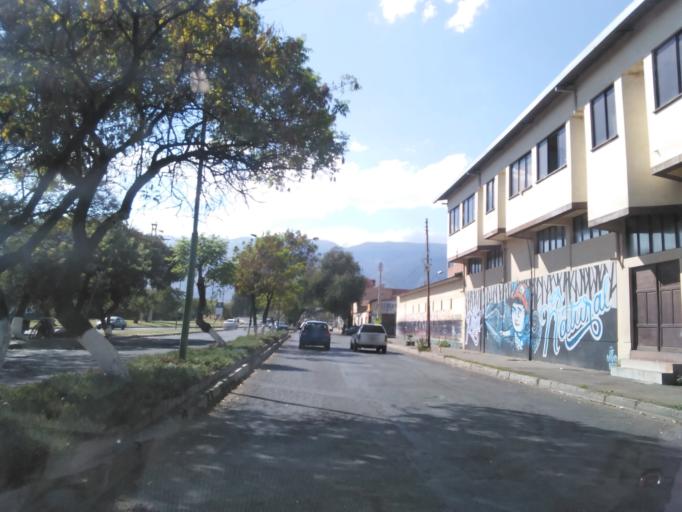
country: BO
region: Cochabamba
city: Cochabamba
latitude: -17.3960
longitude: -66.1670
